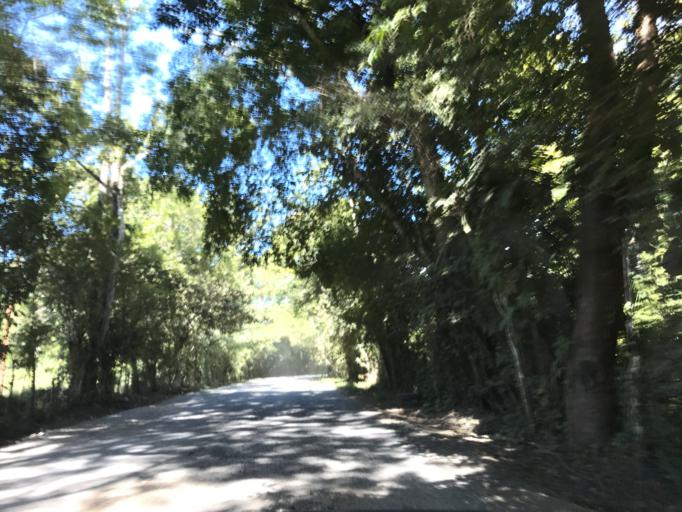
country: GT
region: Izabal
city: Morales
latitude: 15.6474
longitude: -89.0113
